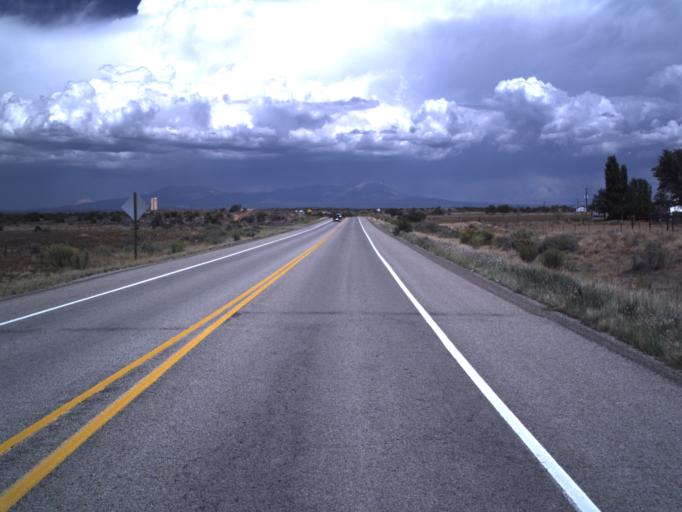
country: US
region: Utah
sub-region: San Juan County
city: Blanding
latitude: 37.4695
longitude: -109.4670
